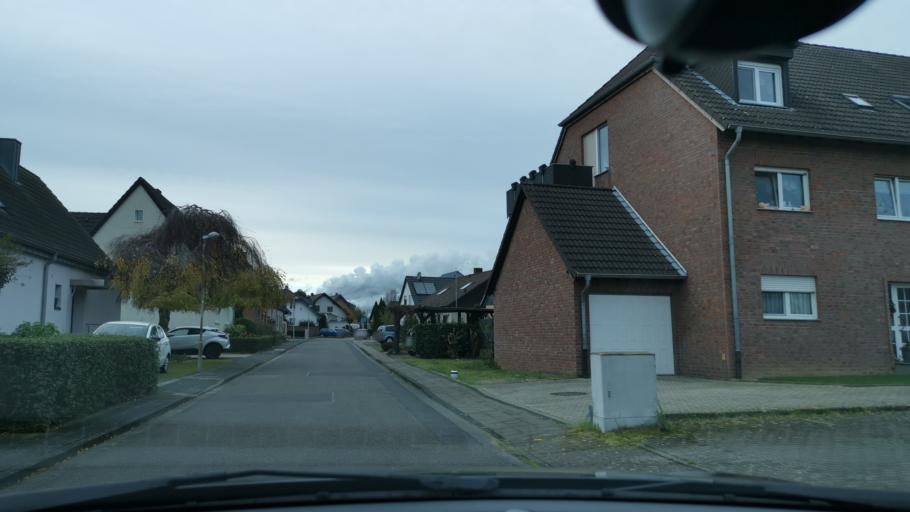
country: DE
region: North Rhine-Westphalia
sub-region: Regierungsbezirk Dusseldorf
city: Rommerskirchen
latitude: 51.0327
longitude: 6.6817
